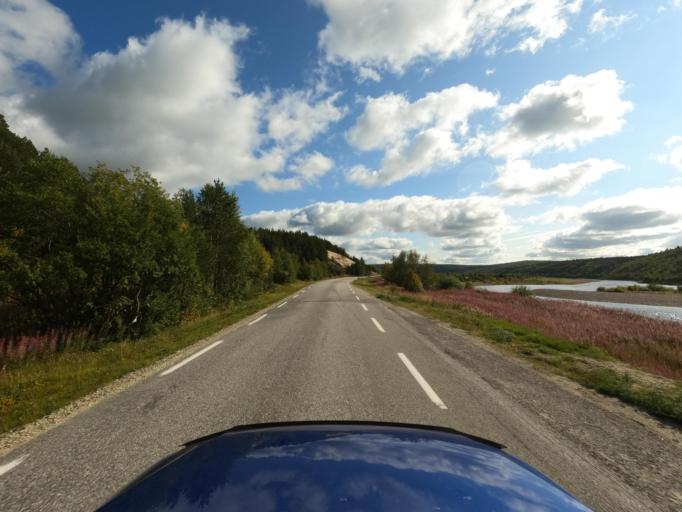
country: NO
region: Finnmark Fylke
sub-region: Karasjok
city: Karasjohka
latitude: 69.4448
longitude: 25.2104
